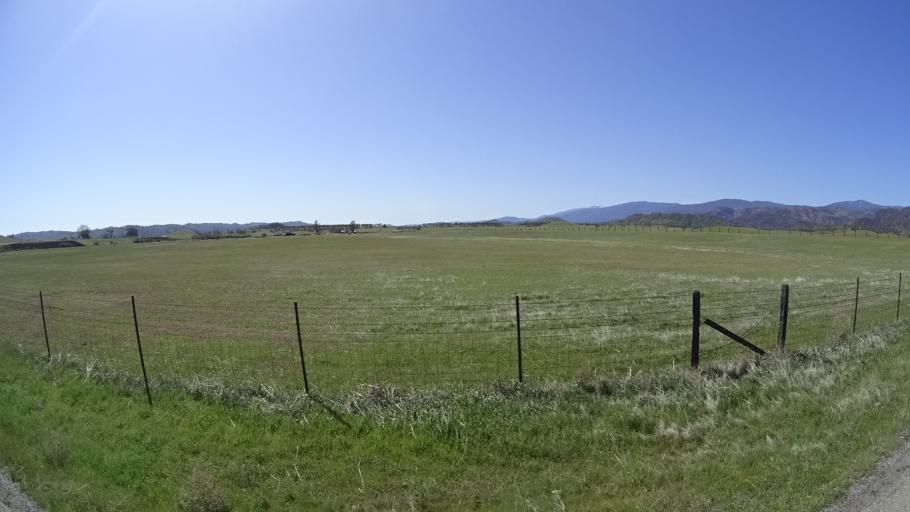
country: US
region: California
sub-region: Tehama County
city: Rancho Tehama Reserve
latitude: 39.6995
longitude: -122.5539
